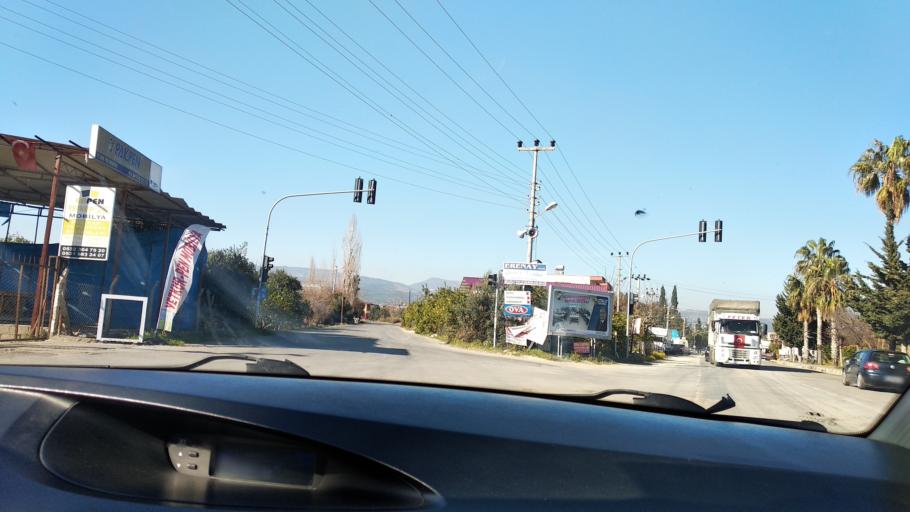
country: TR
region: Mersin
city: Tomuk
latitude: 36.6615
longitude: 34.3647
